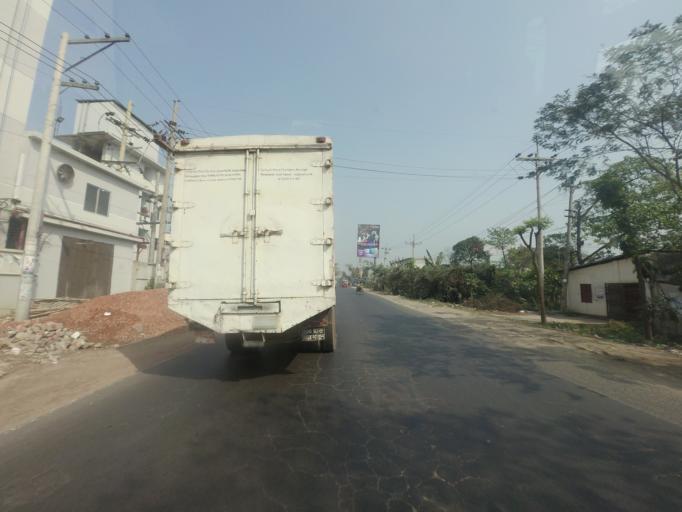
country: BD
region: Dhaka
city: Narsingdi
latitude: 23.8803
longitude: 90.6668
